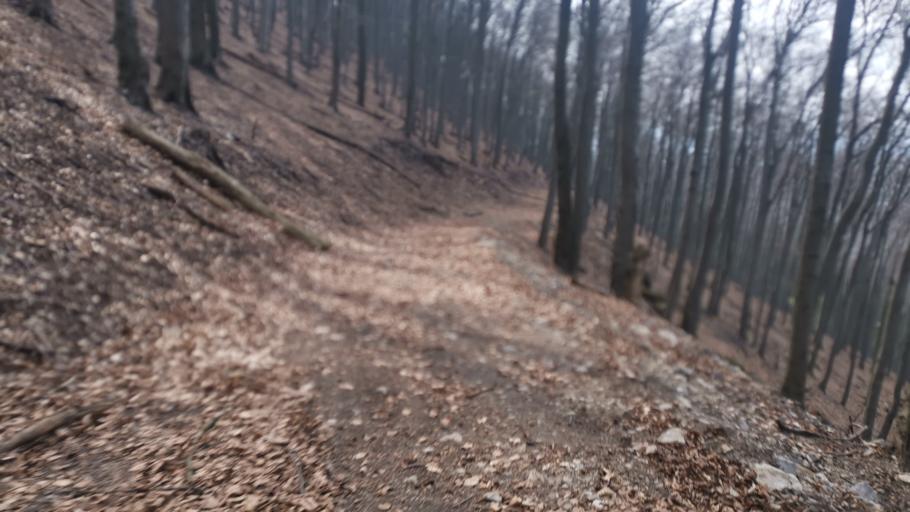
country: SK
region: Trnavsky
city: Smolenice
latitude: 48.5258
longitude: 17.3884
